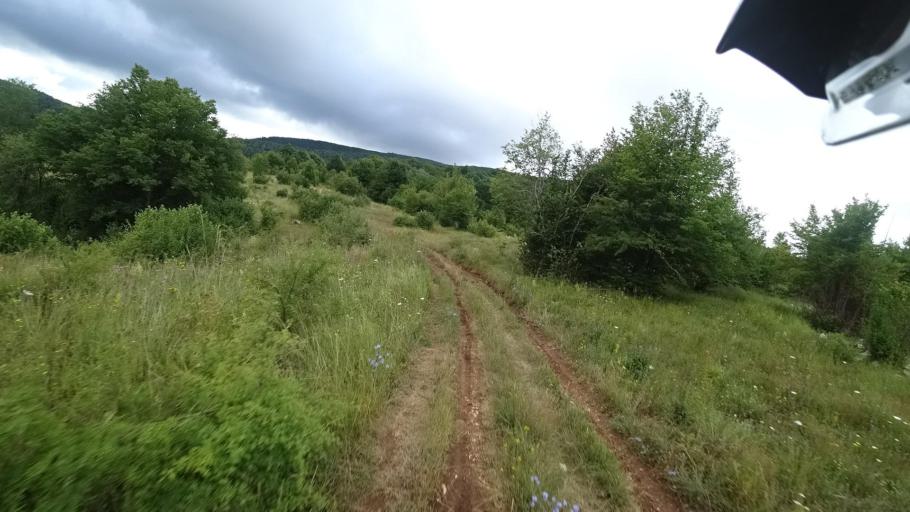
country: HR
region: Licko-Senjska
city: Jezerce
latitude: 44.7628
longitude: 15.4877
